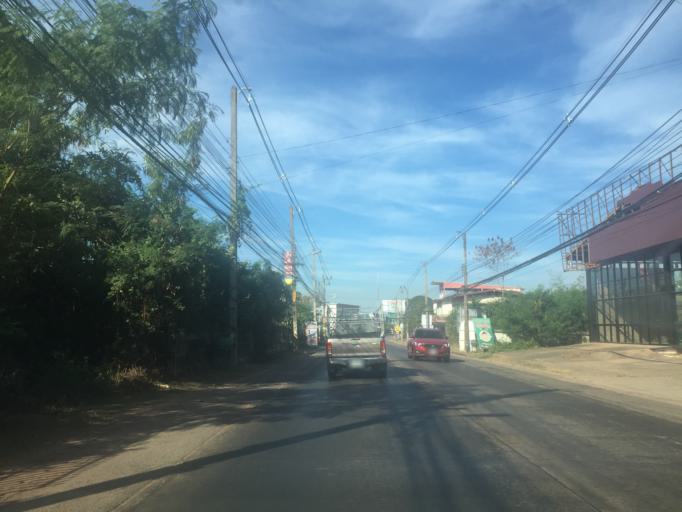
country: TH
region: Changwat Udon Thani
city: Kumphawapi
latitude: 17.1112
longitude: 103.0100
